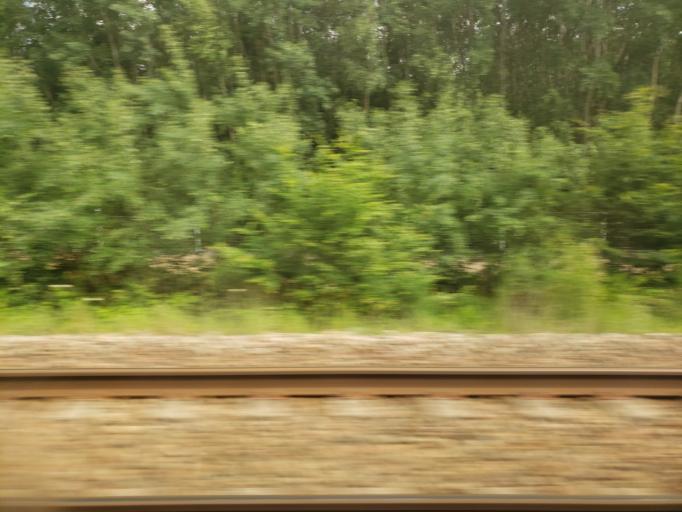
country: FR
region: Ile-de-France
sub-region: Departement de Seine-et-Marne
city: Liverdy-en-Brie
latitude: 48.7184
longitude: 2.7709
